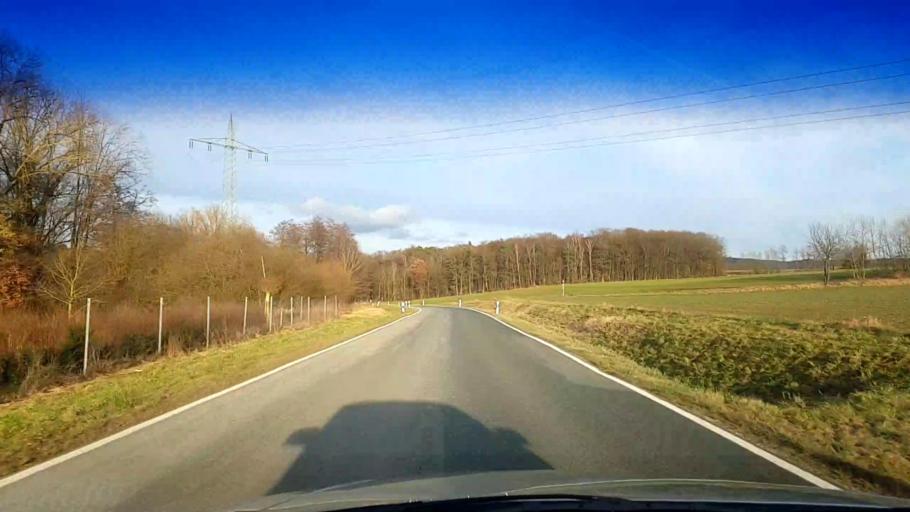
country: DE
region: Bavaria
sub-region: Upper Franconia
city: Hirschaid
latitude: 49.8366
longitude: 10.9959
